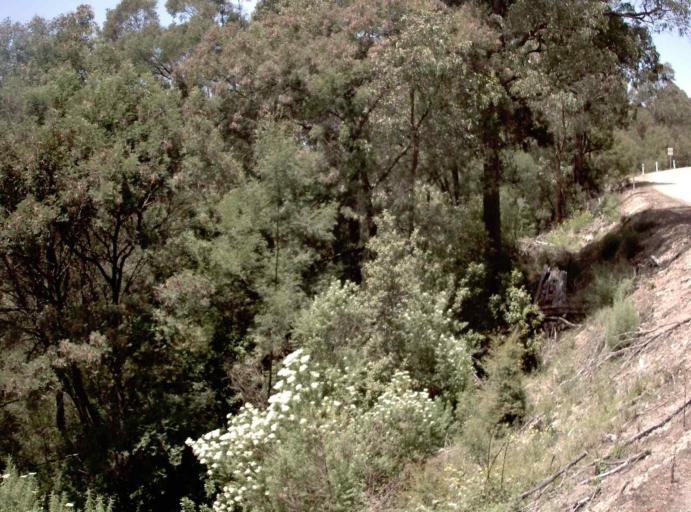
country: AU
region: Victoria
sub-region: East Gippsland
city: Lakes Entrance
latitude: -37.5622
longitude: 147.8872
